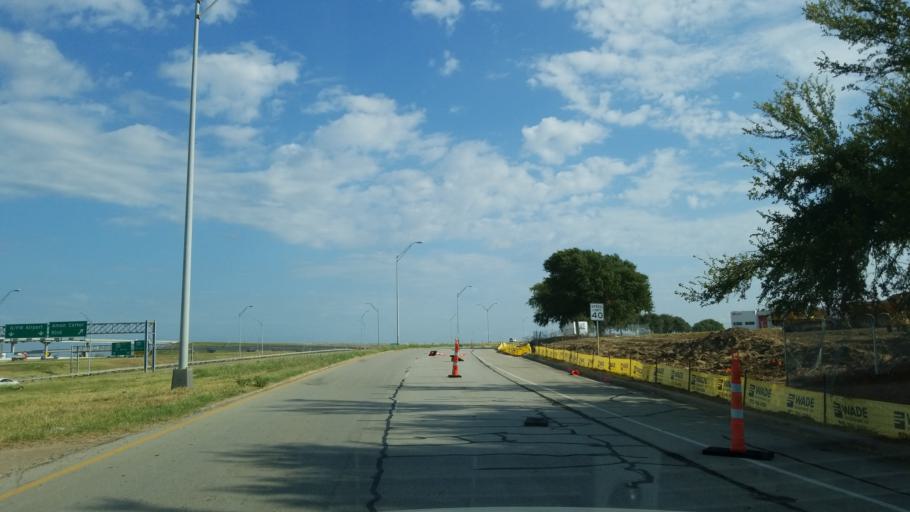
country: US
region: Texas
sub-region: Tarrant County
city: Euless
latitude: 32.8329
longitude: -97.0601
